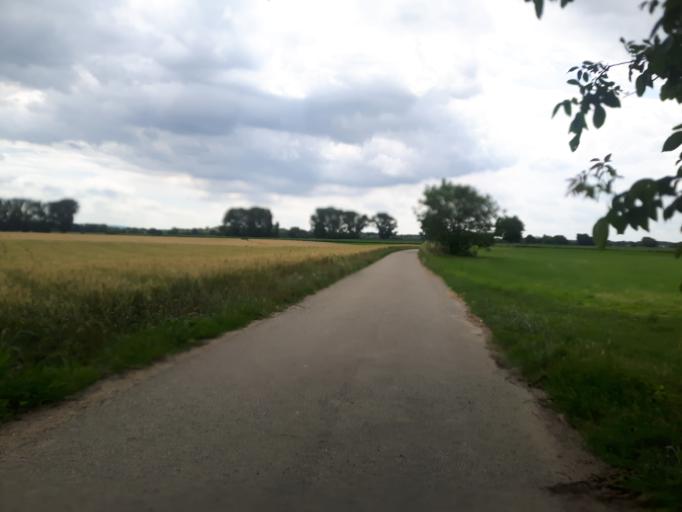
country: DE
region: Rheinland-Pfalz
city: Waldsee
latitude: 49.3887
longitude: 8.4416
